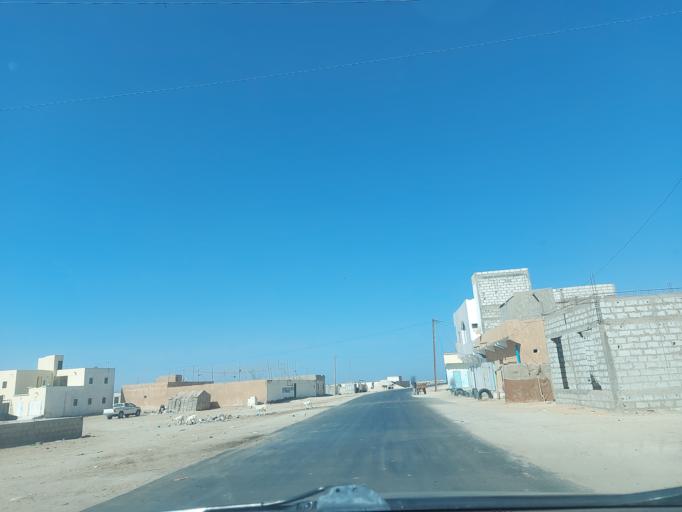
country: MR
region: Nouakchott
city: Nouakchott
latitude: 18.0612
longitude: -16.0057
